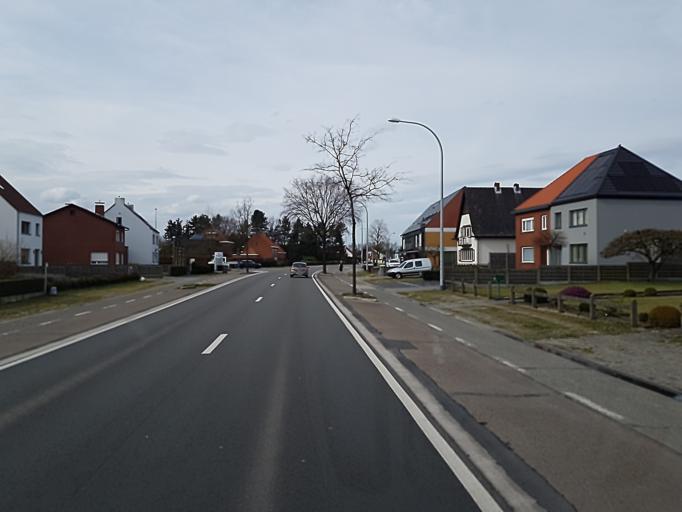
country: BE
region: Flanders
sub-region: Provincie Antwerpen
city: Dessel
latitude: 51.2467
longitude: 5.1090
